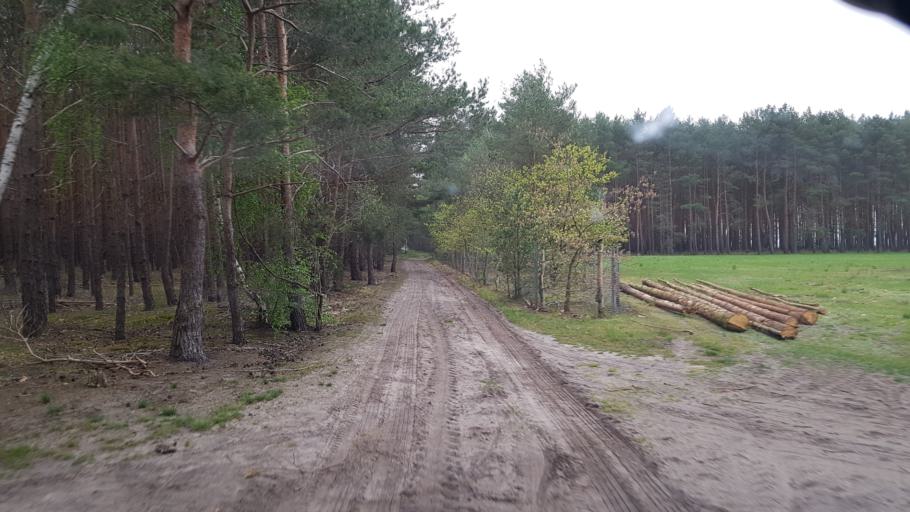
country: DE
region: Brandenburg
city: Schonewalde
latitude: 51.7086
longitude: 13.5611
